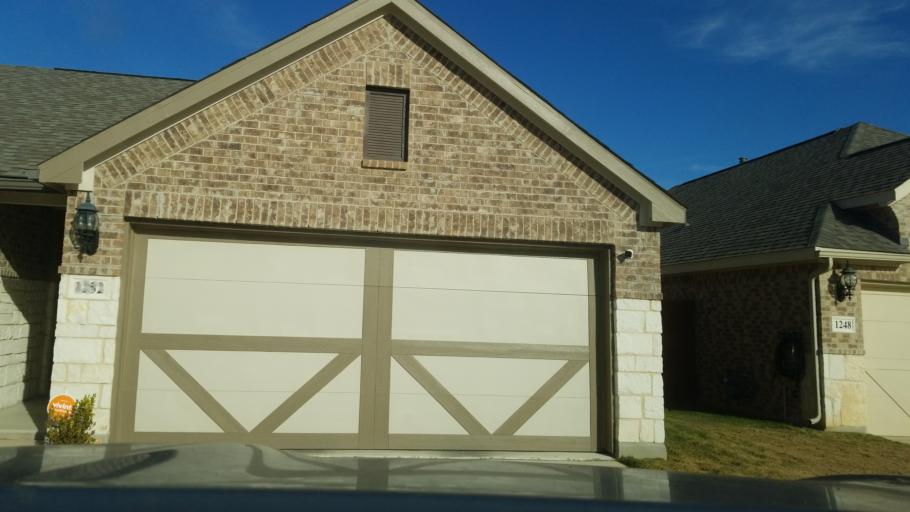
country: US
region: Texas
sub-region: Comal County
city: Canyon Lake
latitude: 29.7775
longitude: -98.2849
